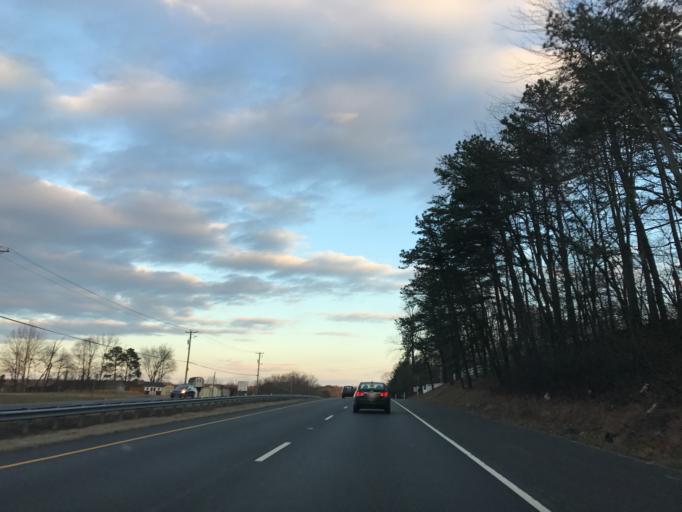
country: US
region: Maryland
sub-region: Cecil County
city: North East
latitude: 39.6098
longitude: -75.8981
